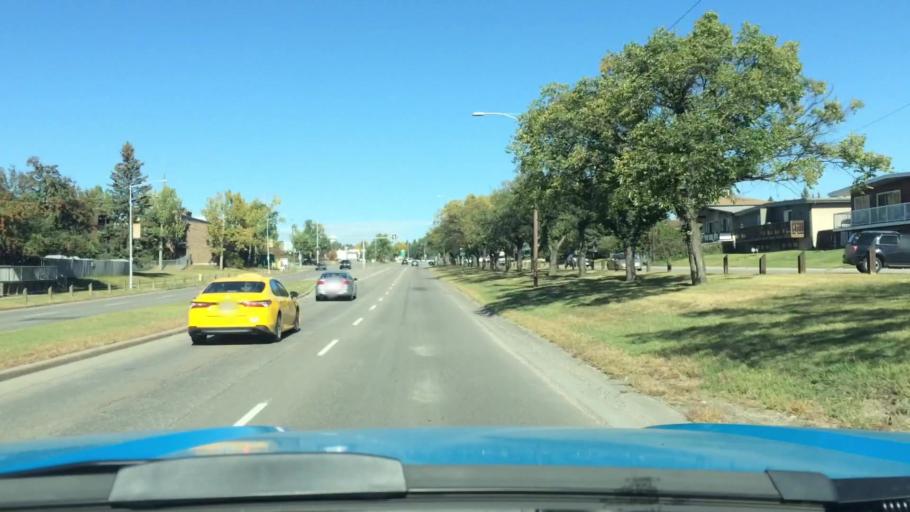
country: CA
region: Alberta
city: Calgary
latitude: 51.1146
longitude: -114.0659
